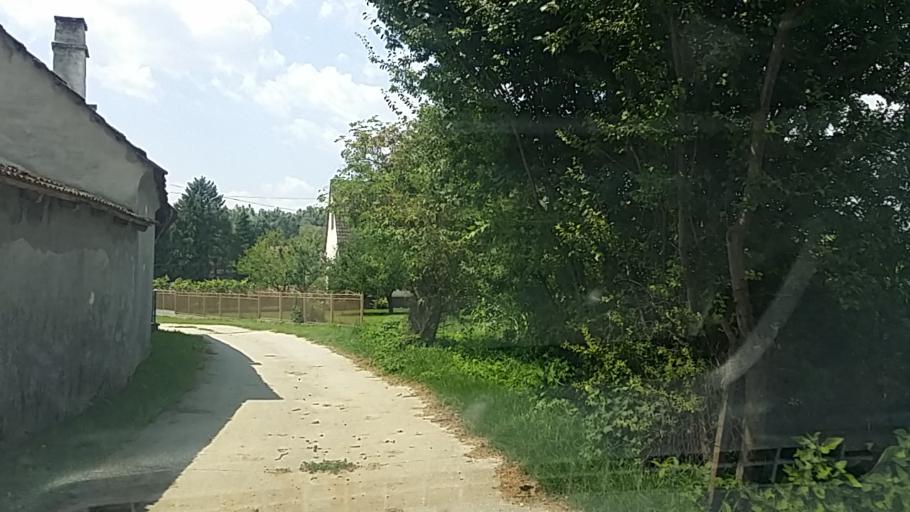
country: HU
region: Zala
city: Murakeresztur
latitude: 46.3500
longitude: 16.8811
